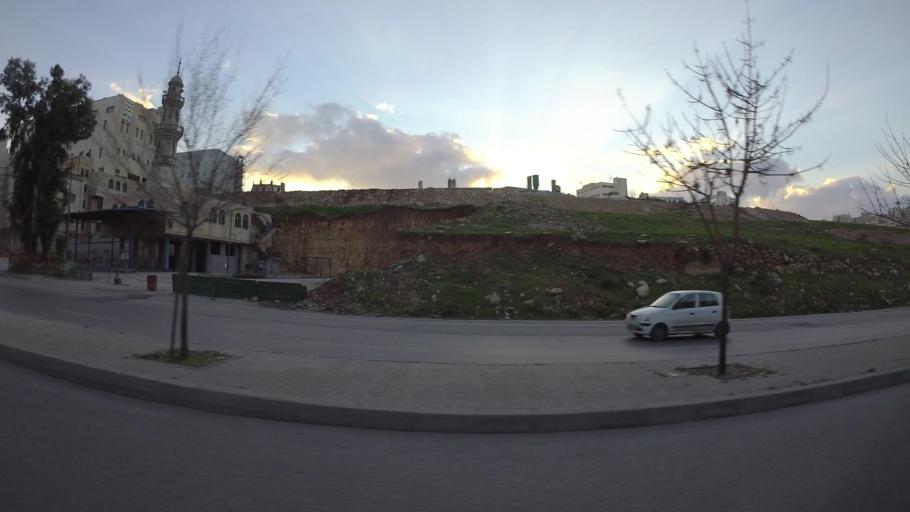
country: JO
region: Amman
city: Al Bunayyat ash Shamaliyah
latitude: 31.9230
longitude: 35.9115
